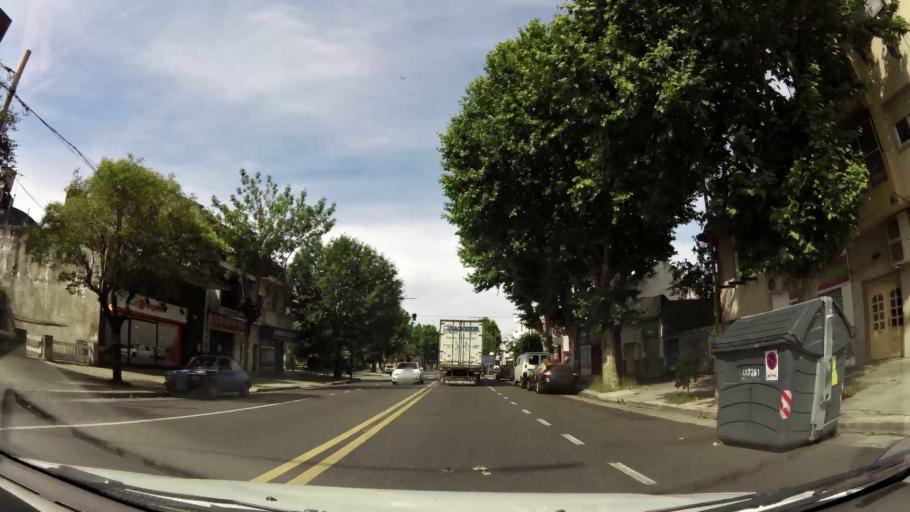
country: AR
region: Buenos Aires F.D.
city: Villa Lugano
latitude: -34.6521
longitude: -58.5159
